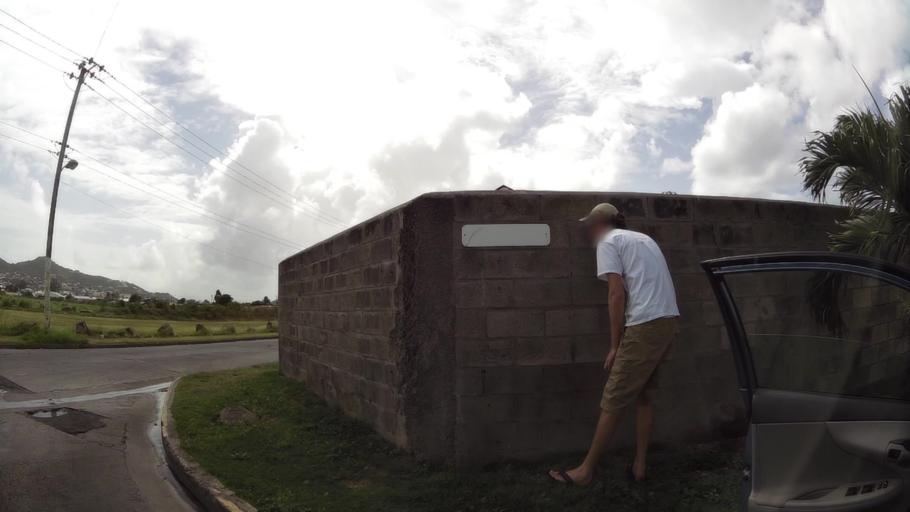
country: KN
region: Saint George Basseterre
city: Basseterre
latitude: 17.2983
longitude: -62.7159
